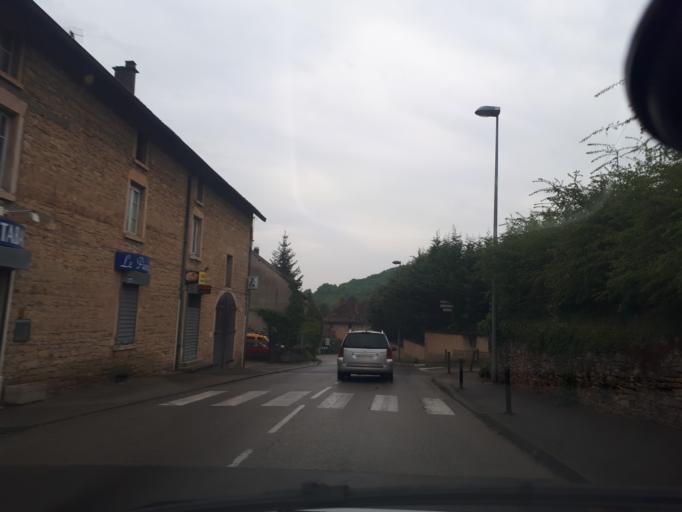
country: FR
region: Rhone-Alpes
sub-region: Departement de l'Isere
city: Frontonas
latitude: 45.6791
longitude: 5.2061
